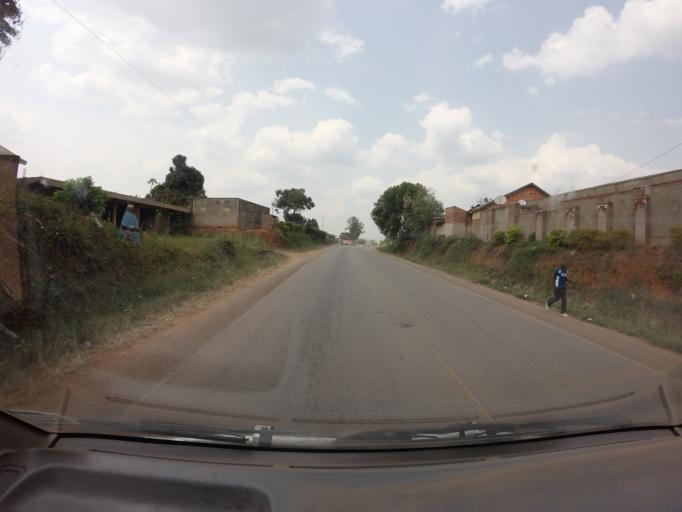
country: UG
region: Central Region
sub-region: Lyantonde District
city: Lyantonde
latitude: -0.4067
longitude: 31.1506
